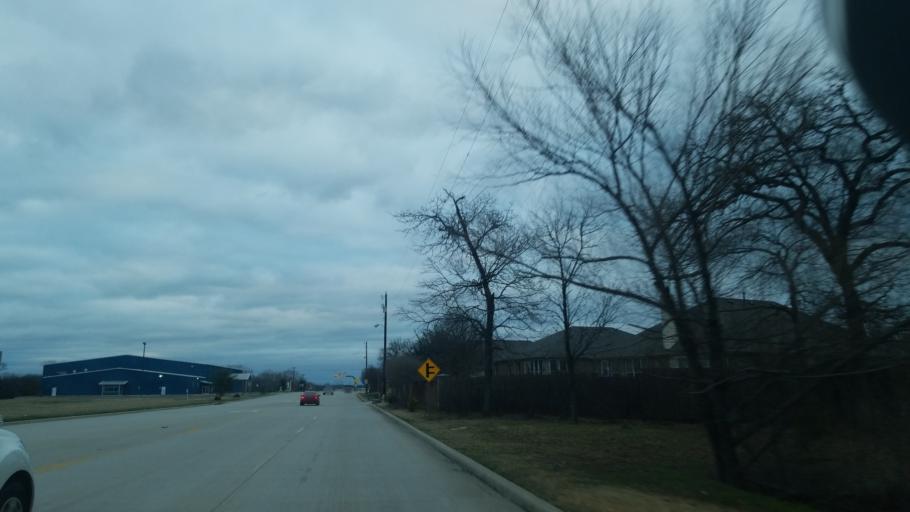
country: US
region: Texas
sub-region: Denton County
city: Lake Dallas
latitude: 33.1319
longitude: -97.0255
